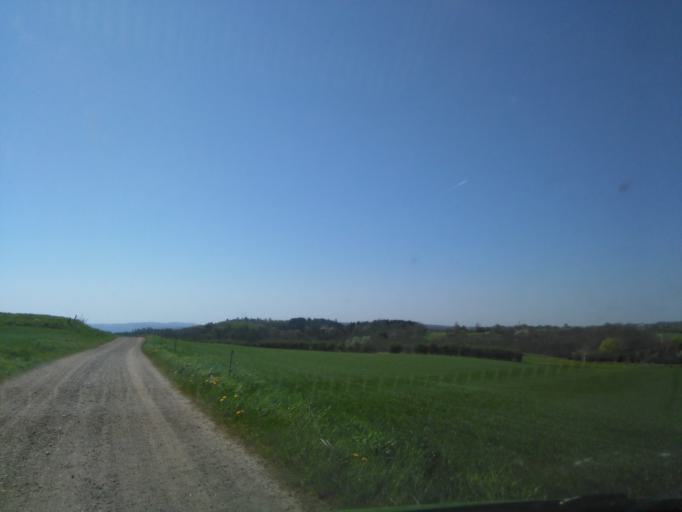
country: DK
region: Central Jutland
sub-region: Odder Kommune
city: Odder
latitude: 55.9005
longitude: 10.0361
